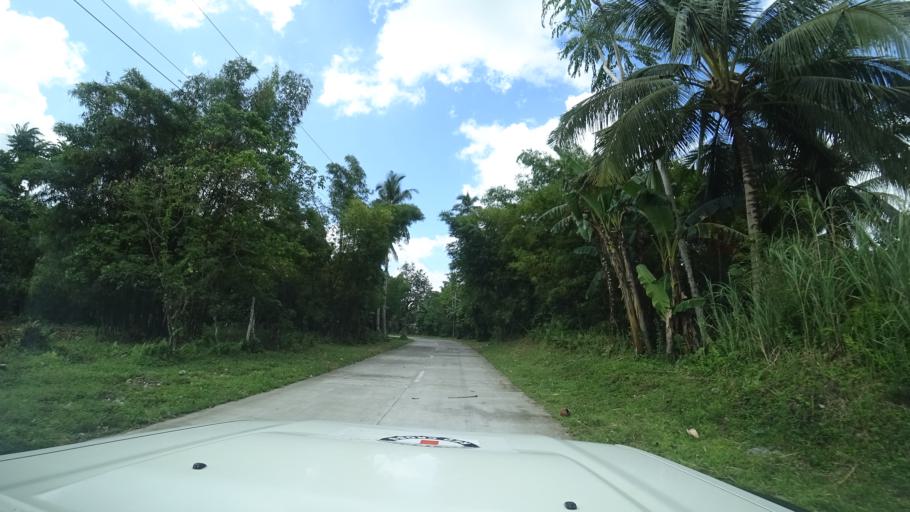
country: PH
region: Eastern Visayas
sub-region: Province of Leyte
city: La Paz
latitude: 10.8699
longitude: 124.9528
